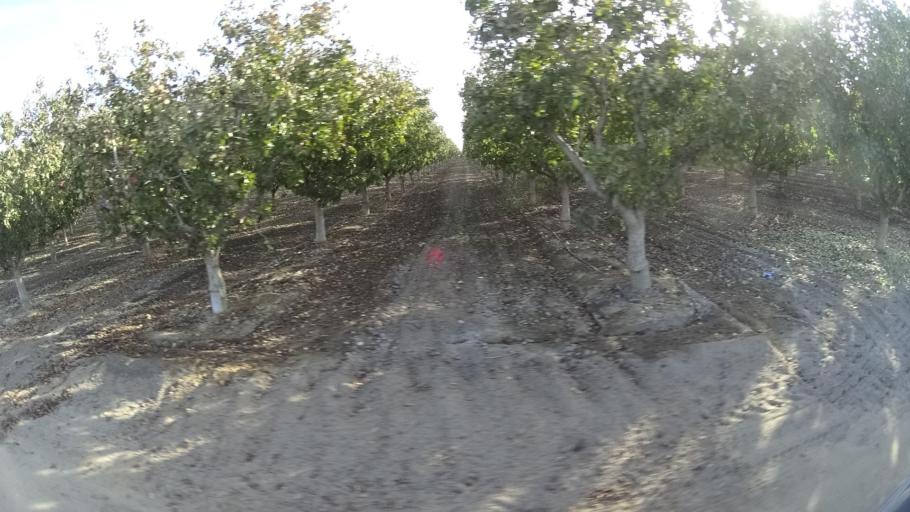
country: US
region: California
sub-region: Kern County
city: McFarland
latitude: 35.7300
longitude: -119.1872
